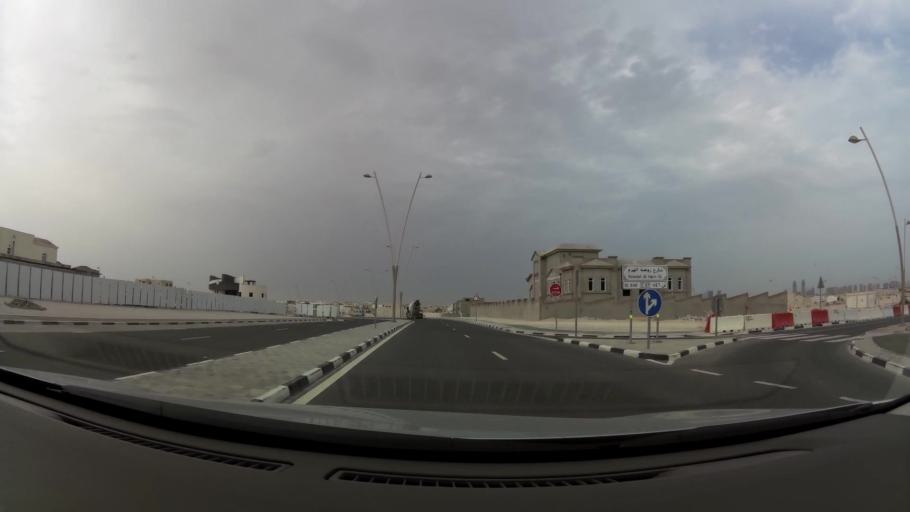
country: QA
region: Baladiyat ad Dawhah
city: Doha
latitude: 25.3410
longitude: 51.4945
